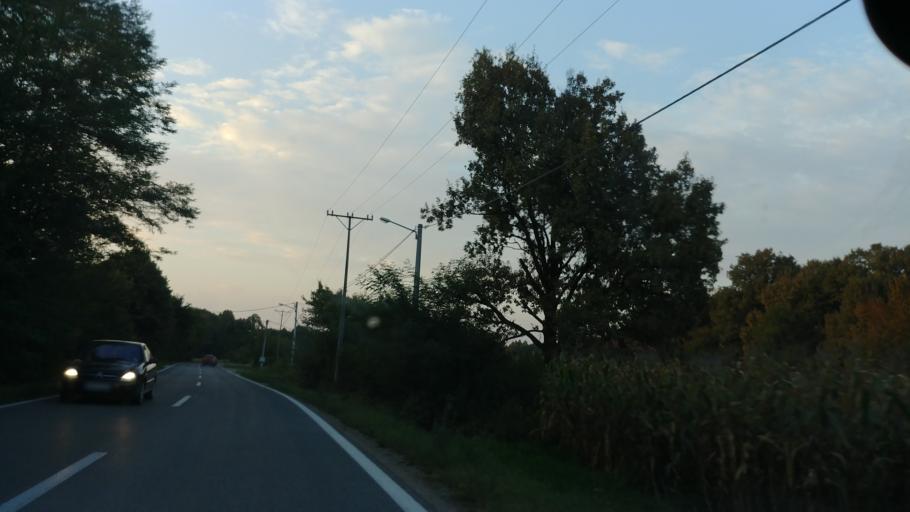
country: BA
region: Brcko
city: Brcko
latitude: 44.7903
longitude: 18.8165
